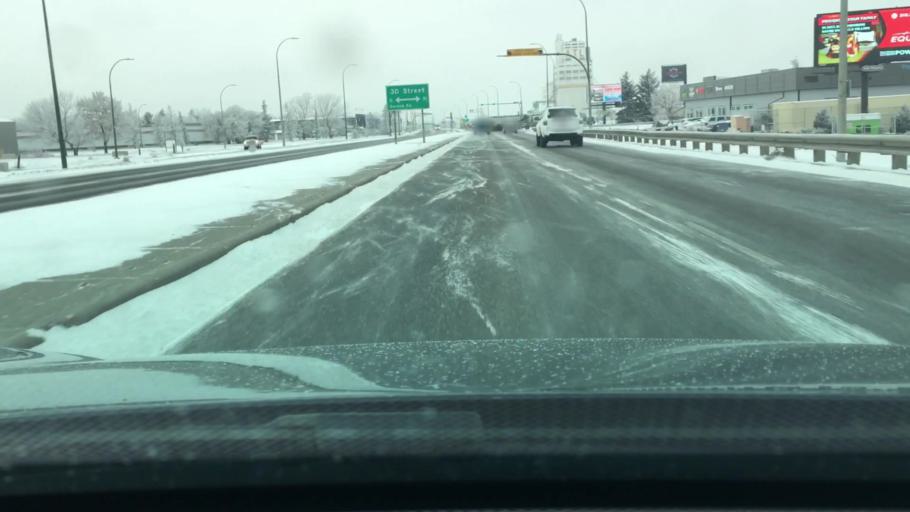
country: CA
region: Alberta
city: Lethbridge
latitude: 49.6983
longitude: -112.7935
